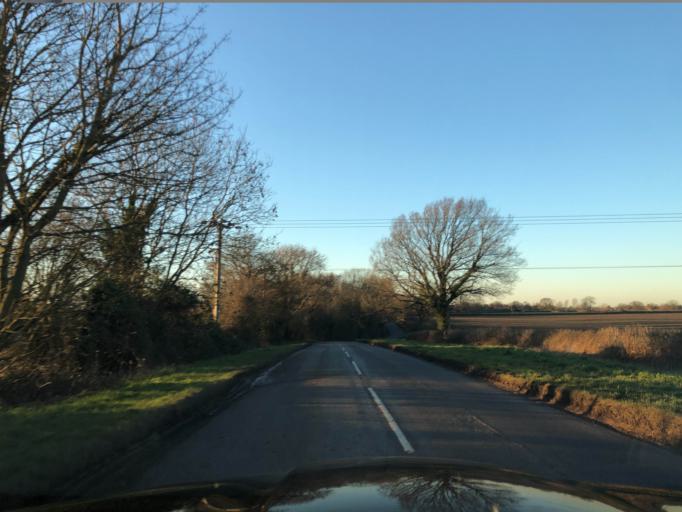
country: GB
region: England
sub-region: Warwickshire
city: Harbury
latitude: 52.2185
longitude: -1.4428
